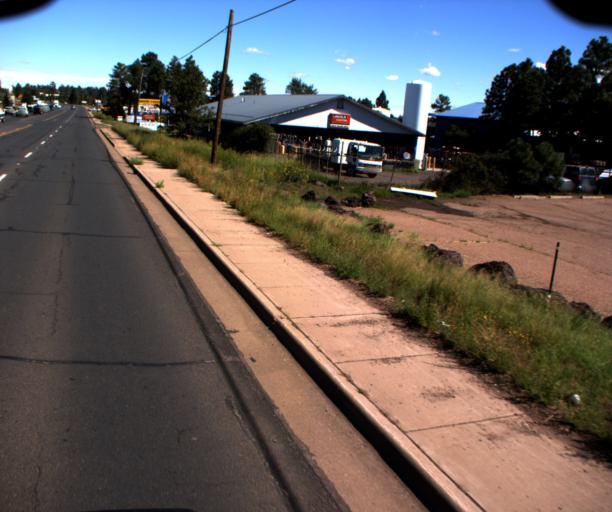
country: US
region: Arizona
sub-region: Navajo County
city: Lake of the Woods
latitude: 34.1882
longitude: -110.0156
